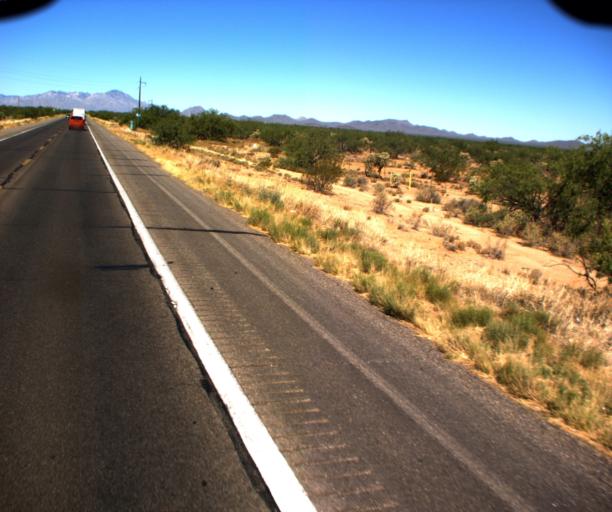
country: US
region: Arizona
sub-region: Pima County
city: Three Points
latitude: 32.1049
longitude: -111.2428
